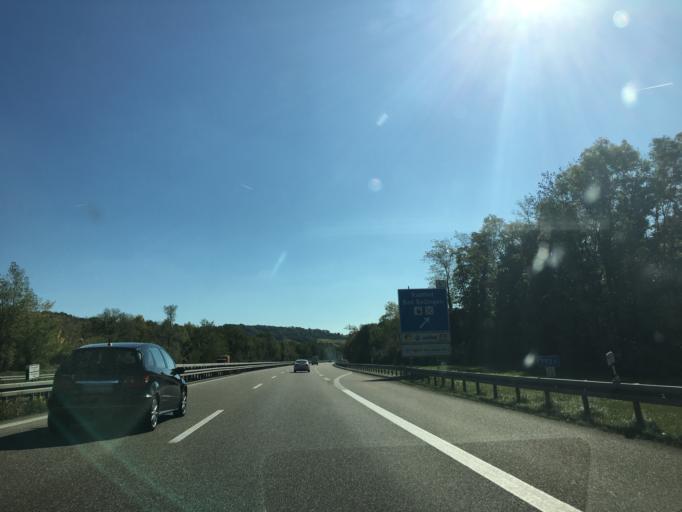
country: DE
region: Baden-Wuerttemberg
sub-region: Freiburg Region
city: Bad Bellingen
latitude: 47.7443
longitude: 7.5514
